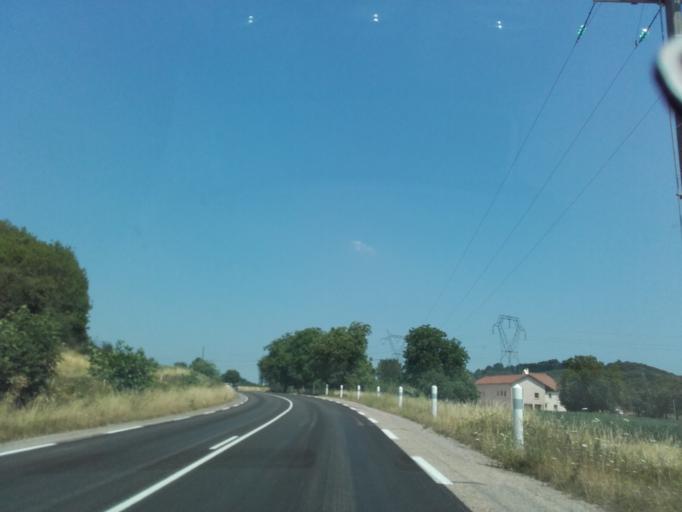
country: FR
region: Rhone-Alpes
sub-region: Departement de l'Isere
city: Champier
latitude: 45.4636
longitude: 5.2932
